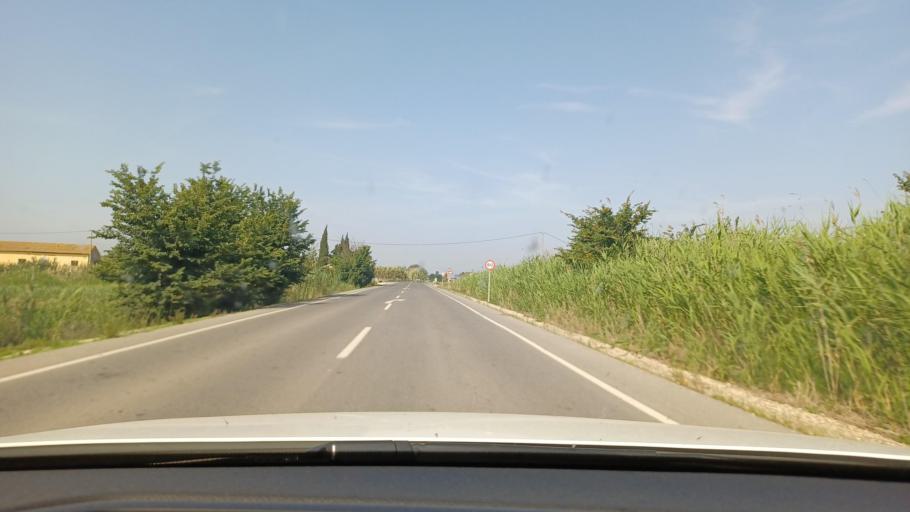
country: ES
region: Valencia
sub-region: Provincia de Alicante
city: Daya Vieja
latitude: 38.1462
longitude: -0.7261
